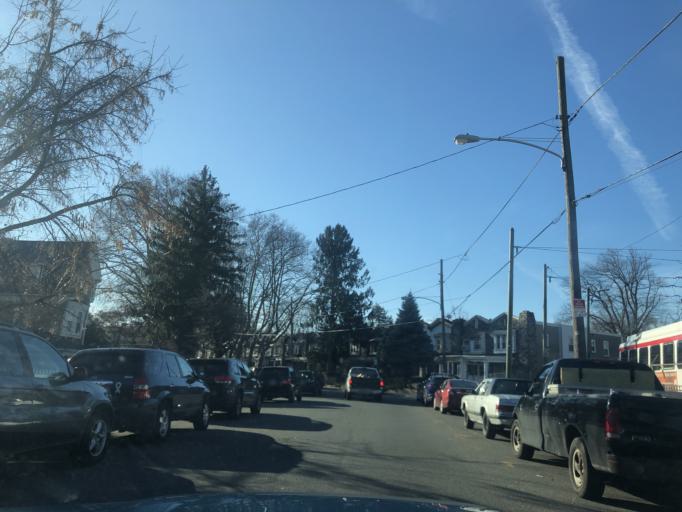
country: US
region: Pennsylvania
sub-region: Delaware County
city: Millbourne
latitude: 39.9840
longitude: -75.2456
